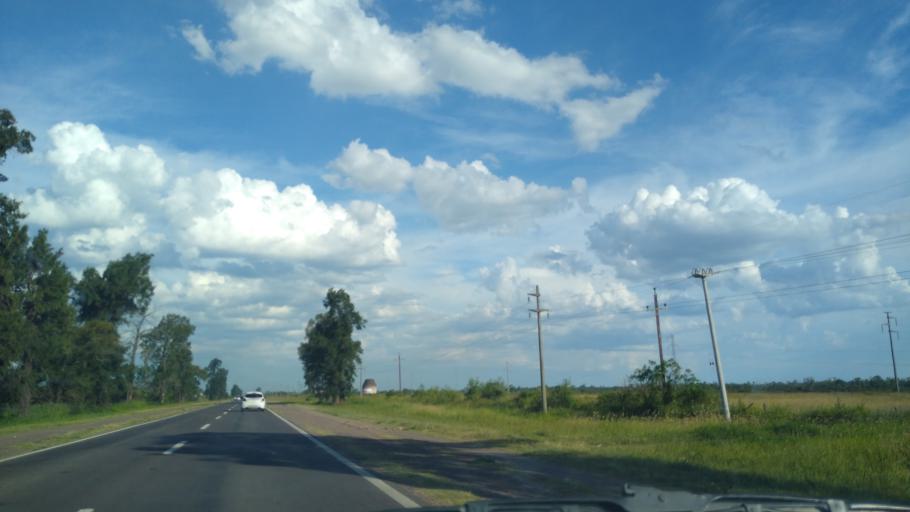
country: AR
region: Chaco
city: Presidencia Roque Saenz Pena
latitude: -26.8200
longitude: -60.3972
